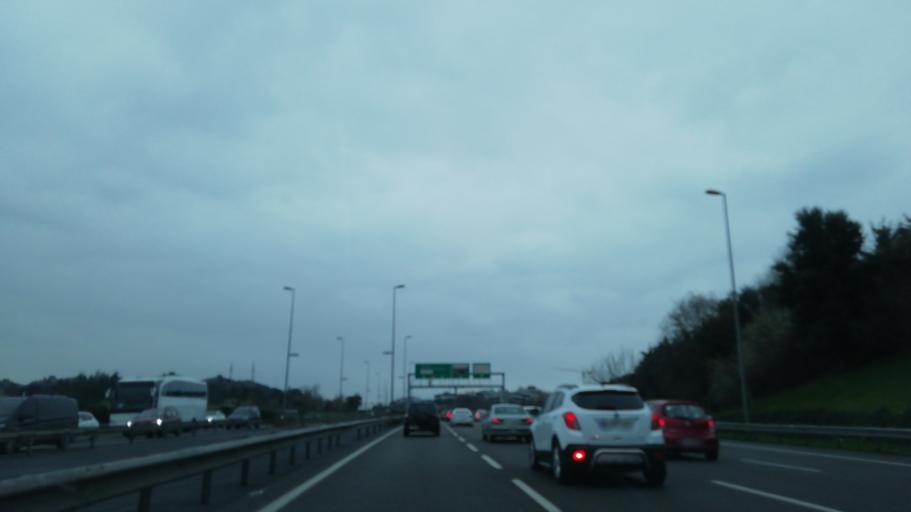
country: TR
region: Istanbul
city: UEskuedar
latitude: 41.0305
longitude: 29.0455
